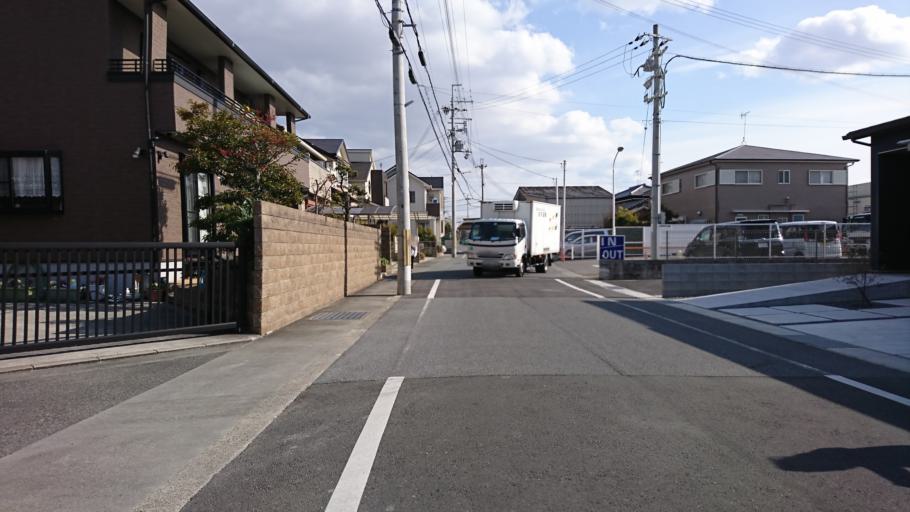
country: JP
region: Hyogo
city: Kakogawacho-honmachi
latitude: 34.7528
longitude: 134.8463
